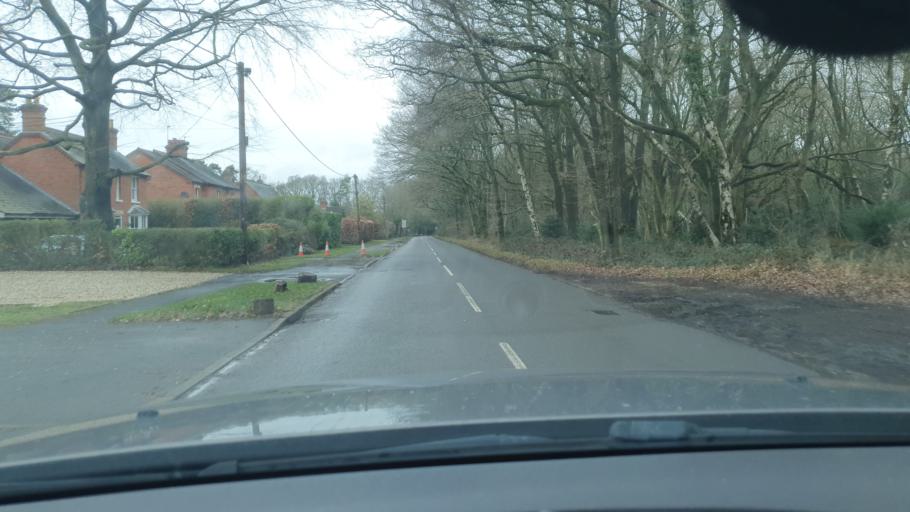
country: GB
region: England
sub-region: West Berkshire
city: Greenham
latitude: 51.3590
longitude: -1.3212
